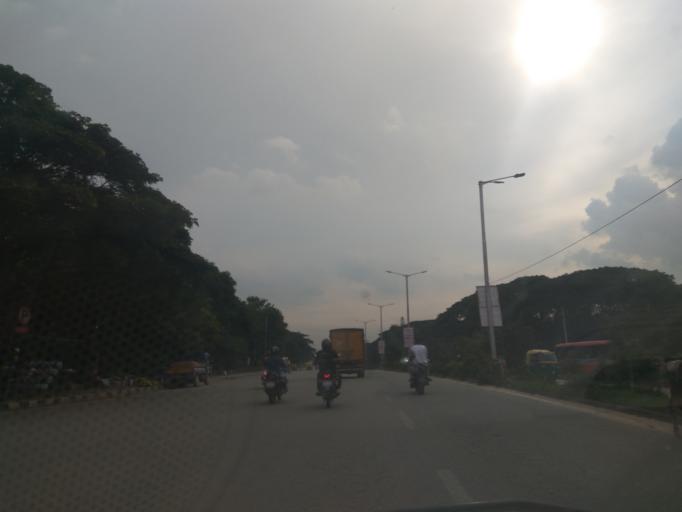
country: IN
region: Karnataka
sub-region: Bangalore Urban
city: Bangalore
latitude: 13.0075
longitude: 77.6898
